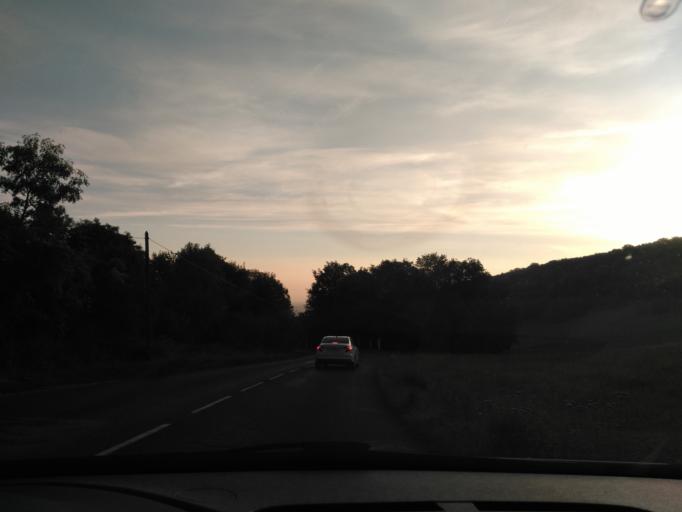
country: FR
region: Rhone-Alpes
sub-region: Departement du Rhone
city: Limonest
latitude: 45.8448
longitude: 4.7942
